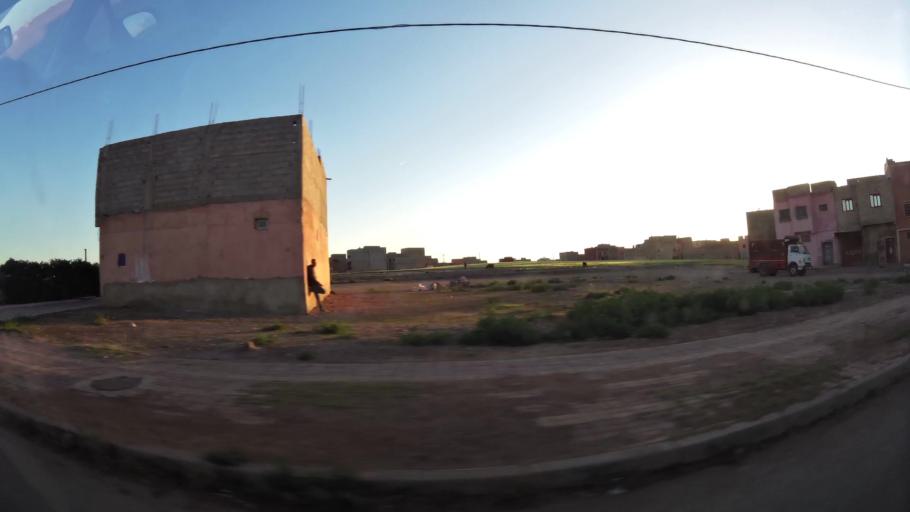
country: MA
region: Marrakech-Tensift-Al Haouz
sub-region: Kelaa-Des-Sraghna
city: Sidi Abdallah
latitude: 32.2417
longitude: -7.9374
